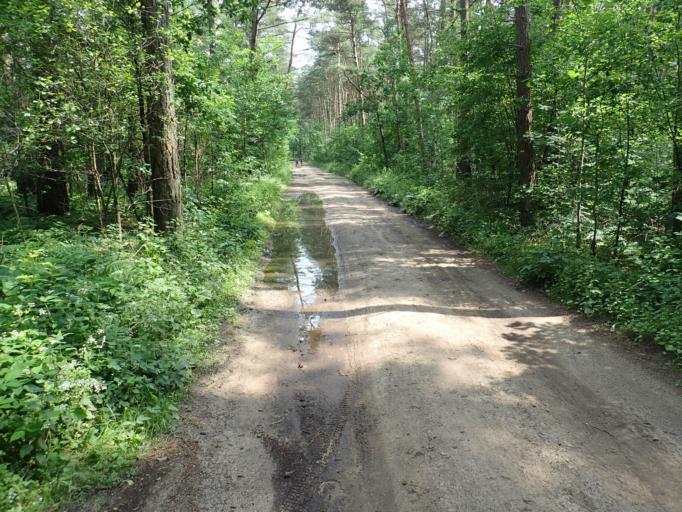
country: BE
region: Flanders
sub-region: Provincie Antwerpen
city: Herentals
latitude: 51.2179
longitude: 4.8910
